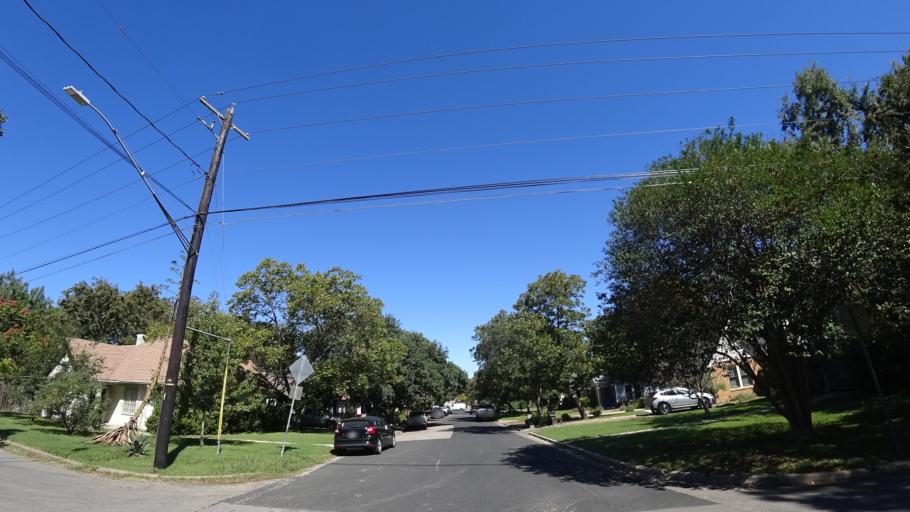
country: US
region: Texas
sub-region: Travis County
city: Austin
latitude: 30.2422
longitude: -97.7415
